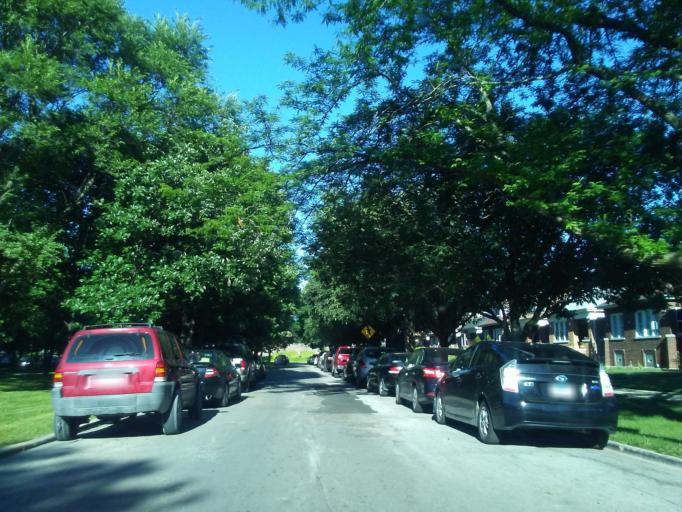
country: US
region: Illinois
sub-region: Cook County
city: Oak Park
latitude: 41.9282
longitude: -87.7439
